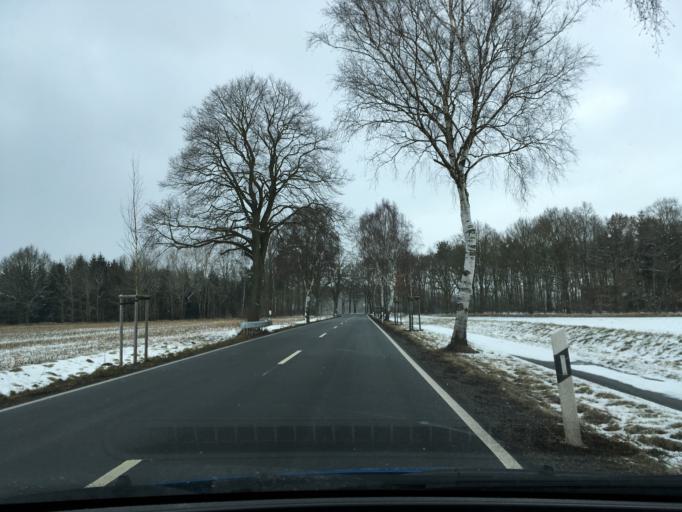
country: DE
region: Lower Saxony
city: Vierhofen
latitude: 53.2855
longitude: 10.2062
